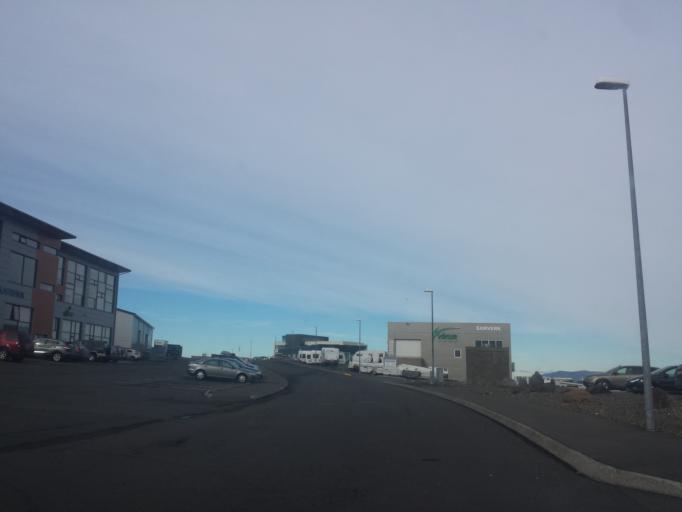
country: IS
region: Capital Region
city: Reykjavik
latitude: 64.0950
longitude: -21.8089
